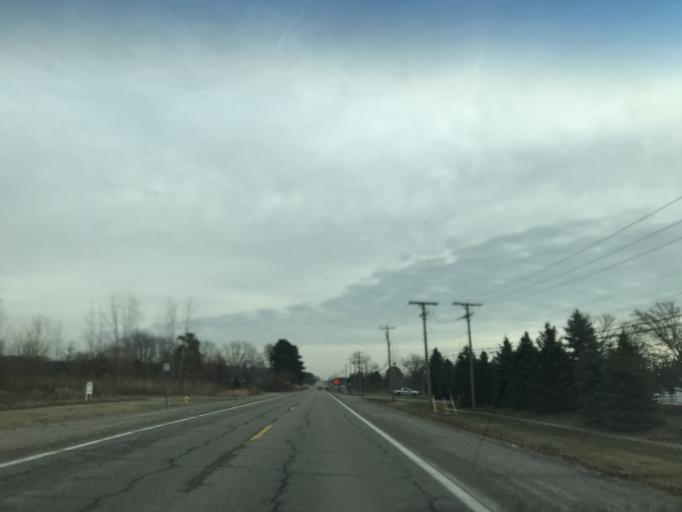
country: US
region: Michigan
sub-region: Macomb County
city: Mount Clemens
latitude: 42.6730
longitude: -82.9043
